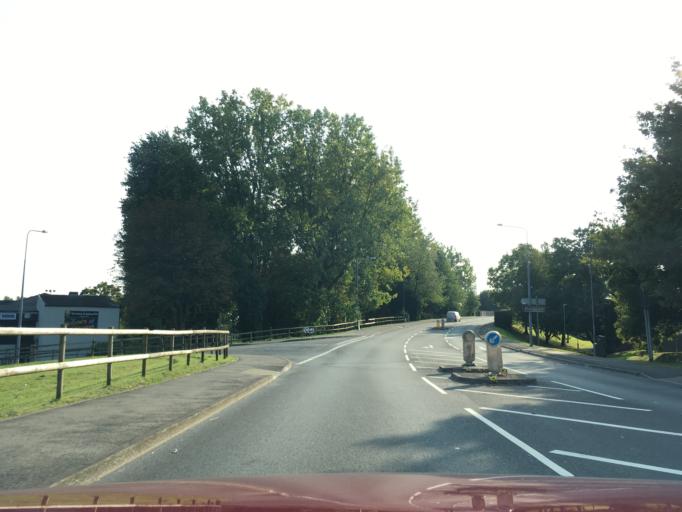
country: GB
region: Wales
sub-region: Torfaen County Borough
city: Cwmbran
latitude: 51.6578
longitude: -3.0139
